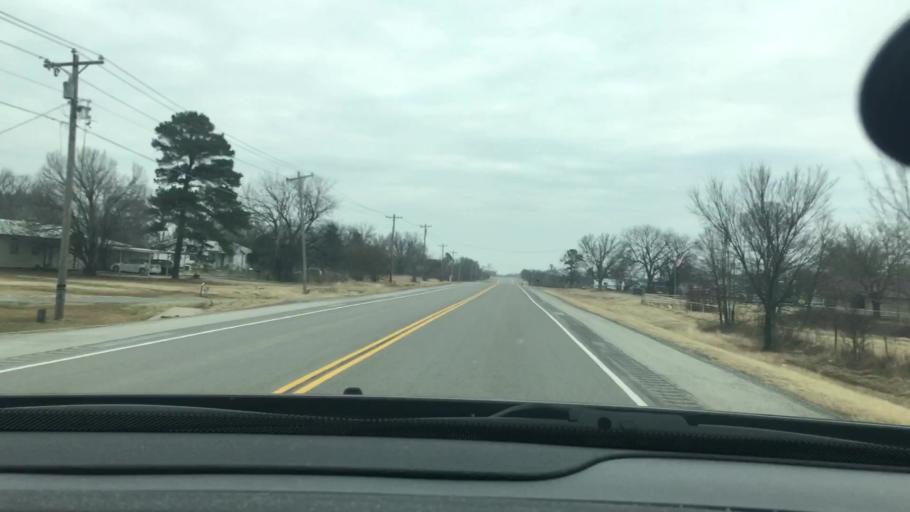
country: US
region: Oklahoma
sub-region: Carter County
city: Healdton
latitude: 34.4047
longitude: -97.5087
